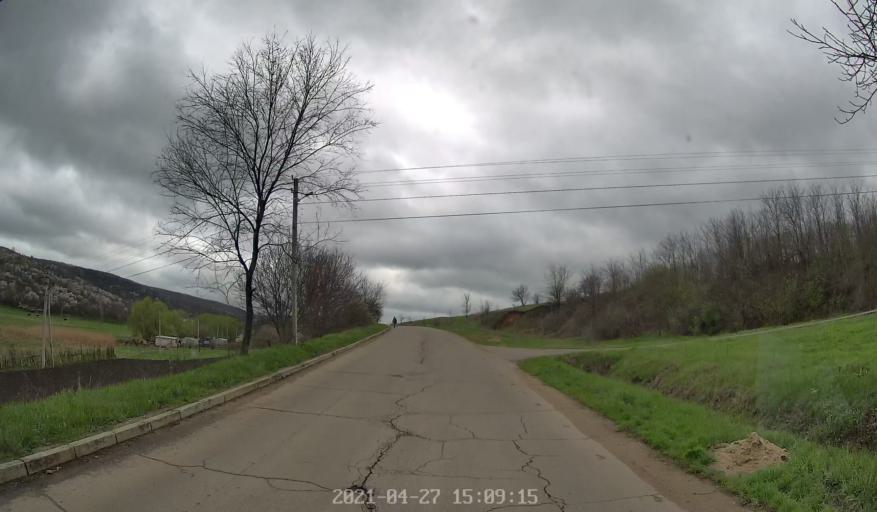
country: MD
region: Chisinau
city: Vadul lui Voda
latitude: 47.0513
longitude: 29.0345
